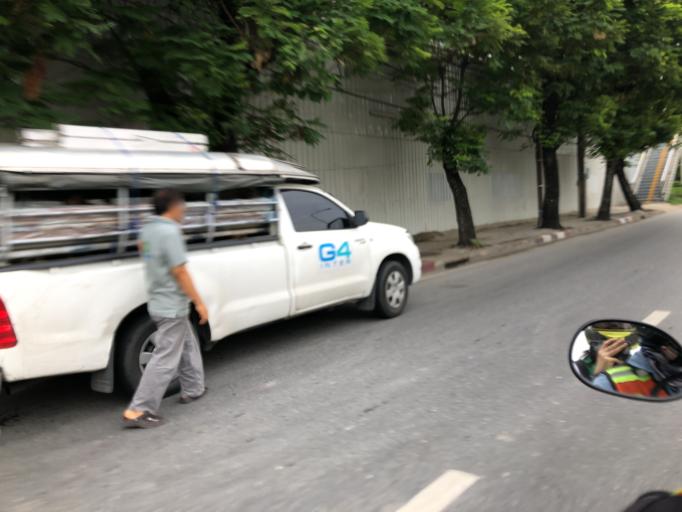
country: TH
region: Bangkok
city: Yan Nawa
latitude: 13.7063
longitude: 100.5383
